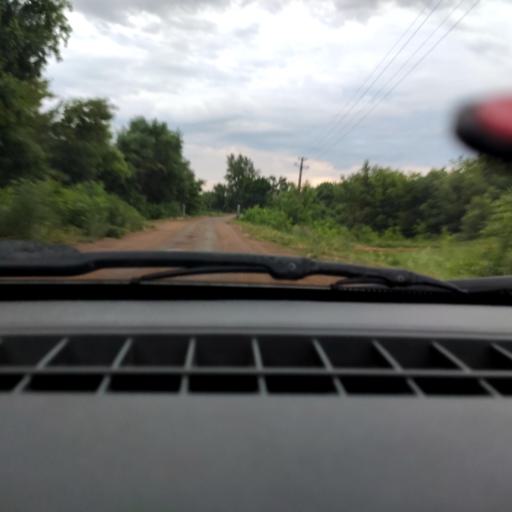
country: RU
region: Bashkortostan
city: Blagoveshchensk
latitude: 54.9277
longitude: 55.9685
